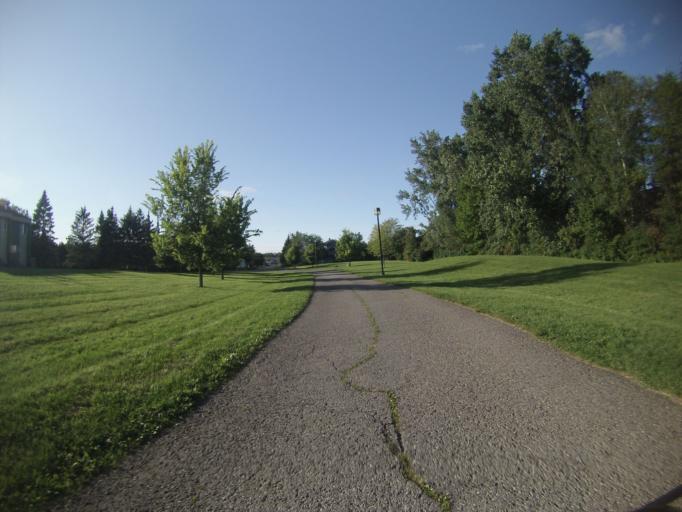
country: CA
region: Ontario
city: Ottawa
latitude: 45.3651
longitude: -75.6365
